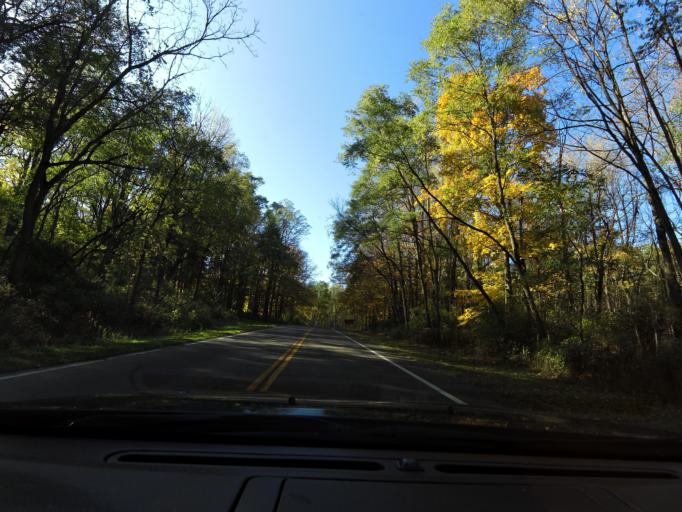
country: US
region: New York
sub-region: Wyoming County
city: Perry
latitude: 42.6952
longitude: -77.9546
